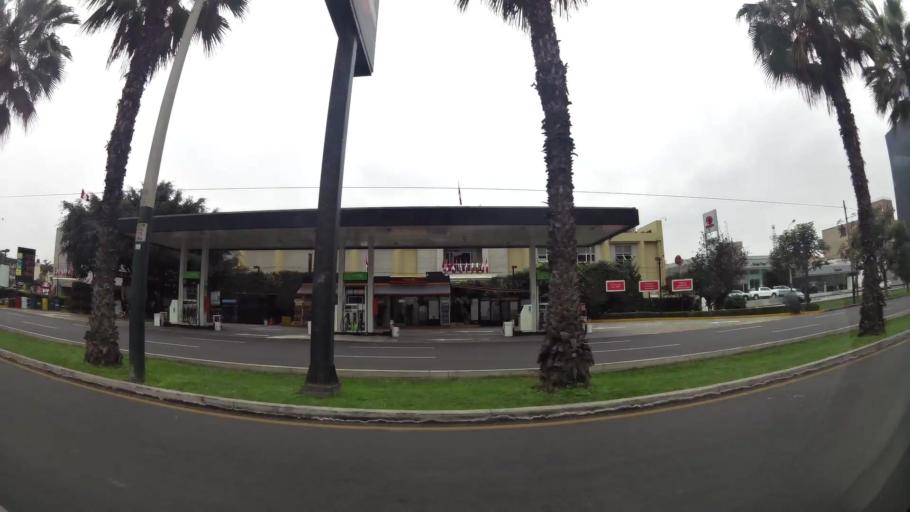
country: PE
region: Lima
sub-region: Lima
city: San Luis
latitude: -12.0964
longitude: -77.0208
